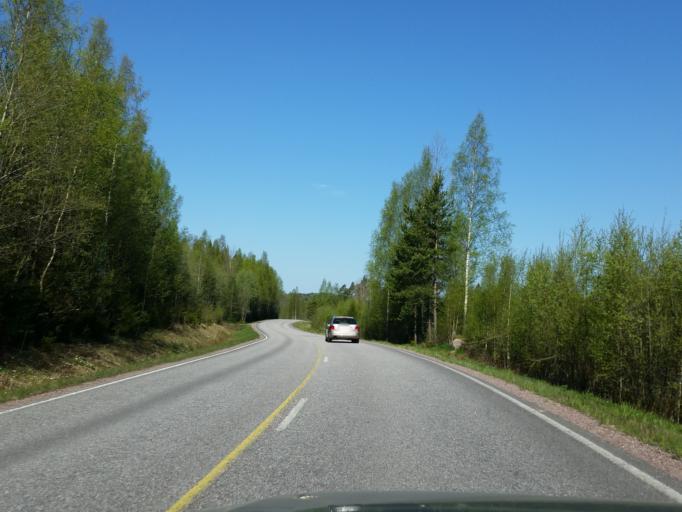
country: FI
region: Uusimaa
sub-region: Helsinki
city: Kirkkonummi
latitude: 60.1950
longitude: 24.3933
